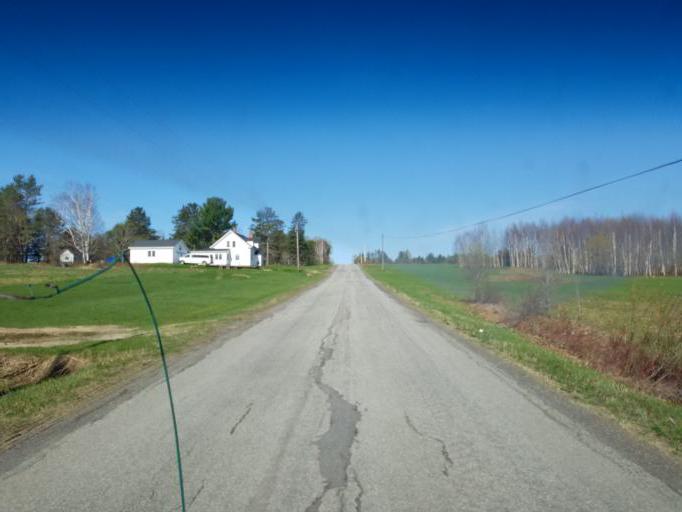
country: US
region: Maine
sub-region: Aroostook County
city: Caribou
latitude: 46.8441
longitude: -68.2066
